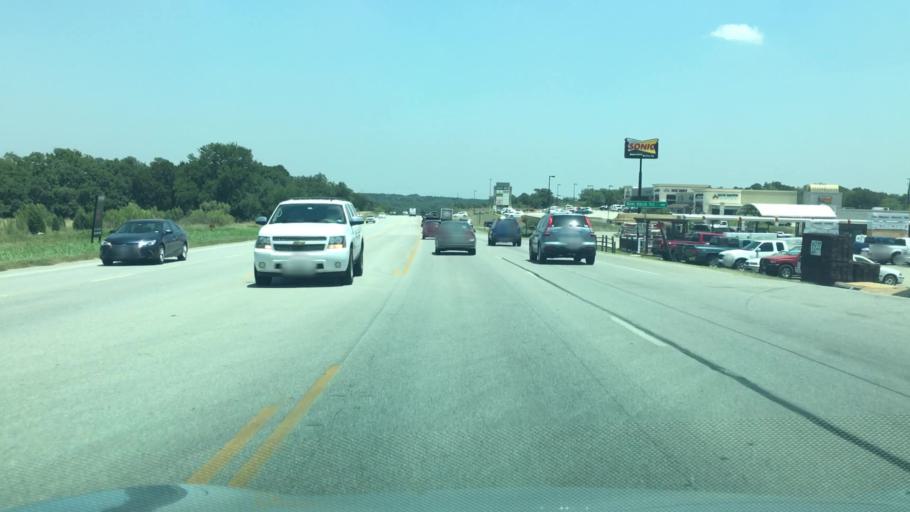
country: US
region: Texas
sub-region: Travis County
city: Bee Cave
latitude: 30.2122
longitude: -97.9668
